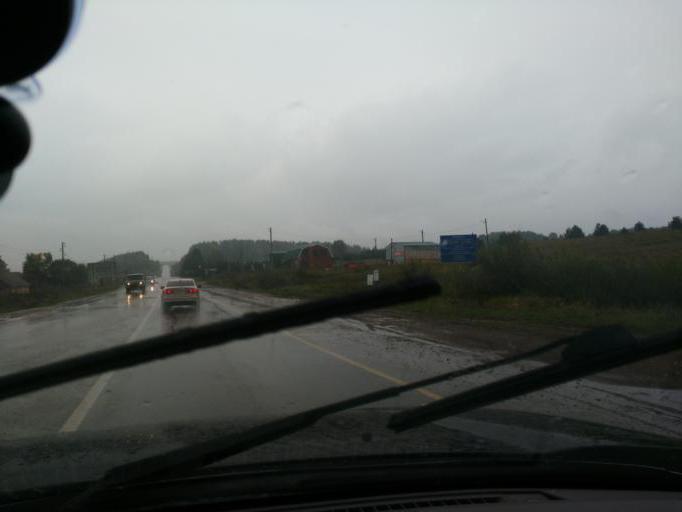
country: RU
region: Perm
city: Osa
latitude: 57.1849
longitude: 55.5906
